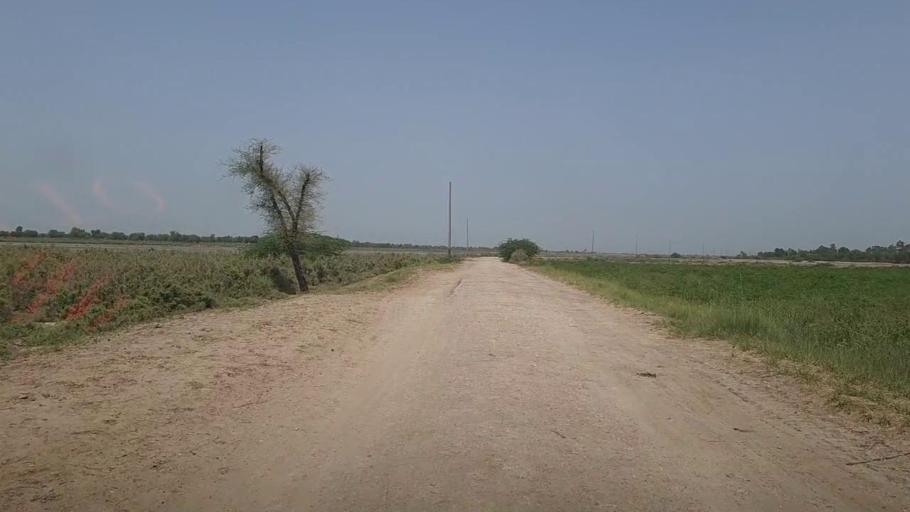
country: PK
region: Sindh
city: Pad Idan
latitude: 26.8520
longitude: 68.2954
